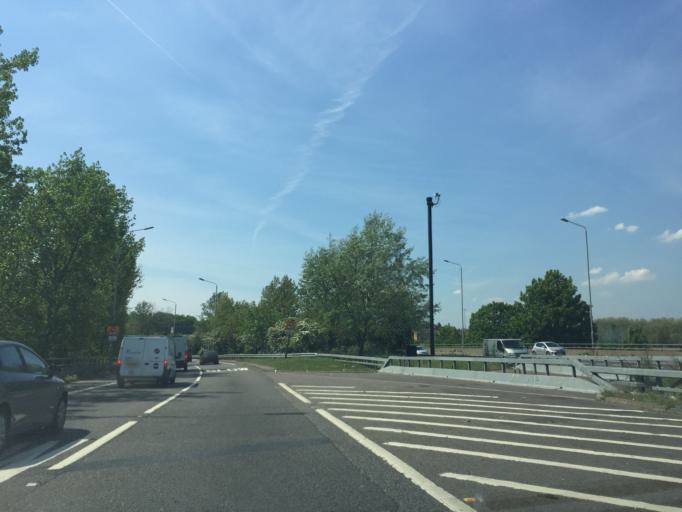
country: GB
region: England
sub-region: Greater London
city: Hackney
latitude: 51.5481
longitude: -0.0283
